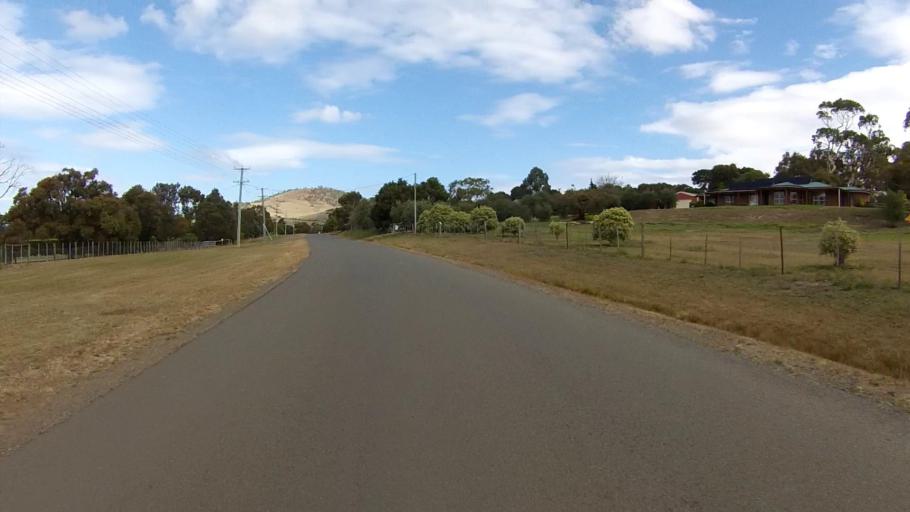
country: AU
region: Tasmania
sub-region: Clarence
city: Acton Park
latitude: -42.8584
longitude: 147.4827
